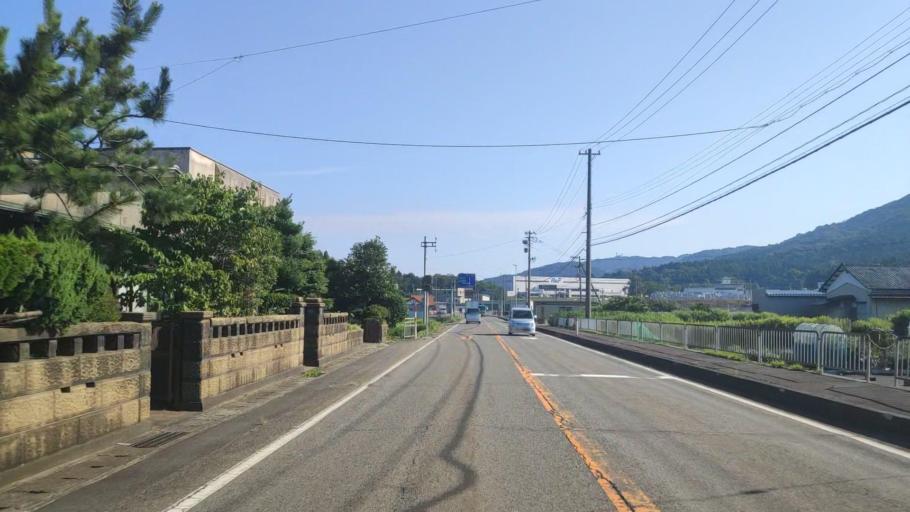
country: JP
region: Fukui
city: Maruoka
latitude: 36.2339
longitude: 136.2868
